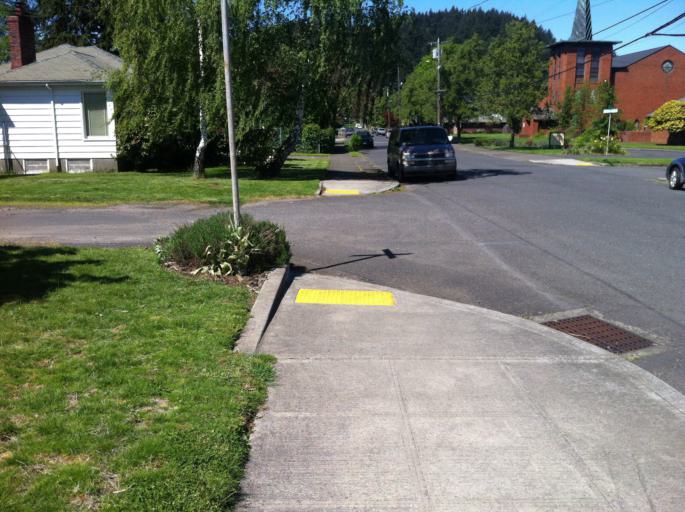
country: US
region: Oregon
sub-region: Multnomah County
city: Lents
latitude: 45.5021
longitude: -122.5948
